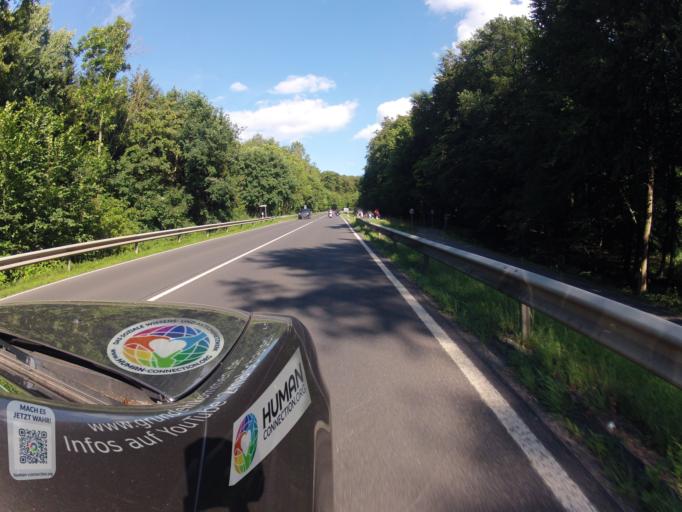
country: DE
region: Mecklenburg-Vorpommern
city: Seebad Bansin
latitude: 53.9763
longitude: 14.1061
